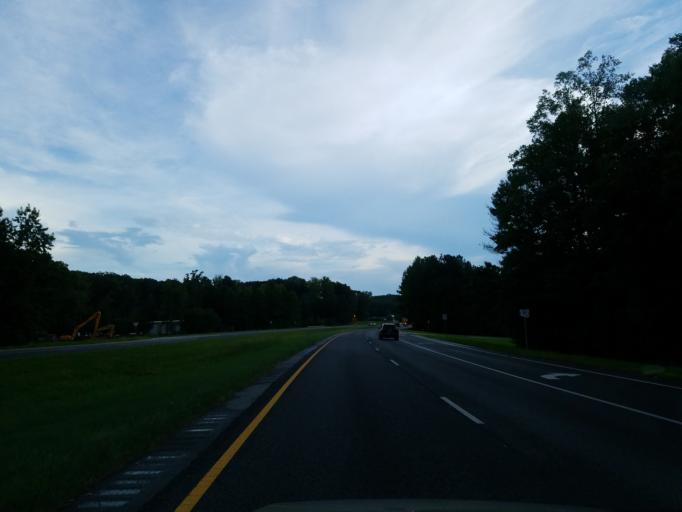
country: US
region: Georgia
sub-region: Forsyth County
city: Cumming
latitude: 34.2757
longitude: -84.0773
